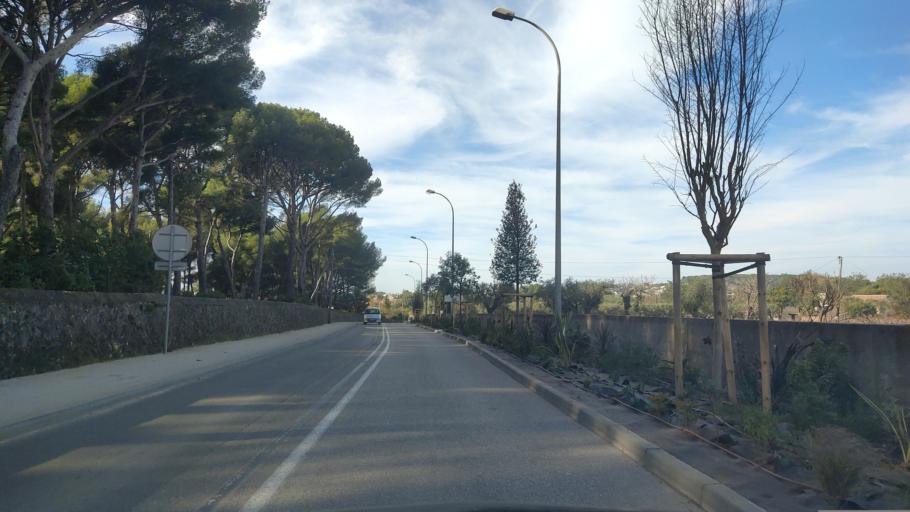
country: FR
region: Provence-Alpes-Cote d'Azur
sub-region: Departement du Var
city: Sanary-sur-Mer
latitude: 43.1273
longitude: 5.8127
